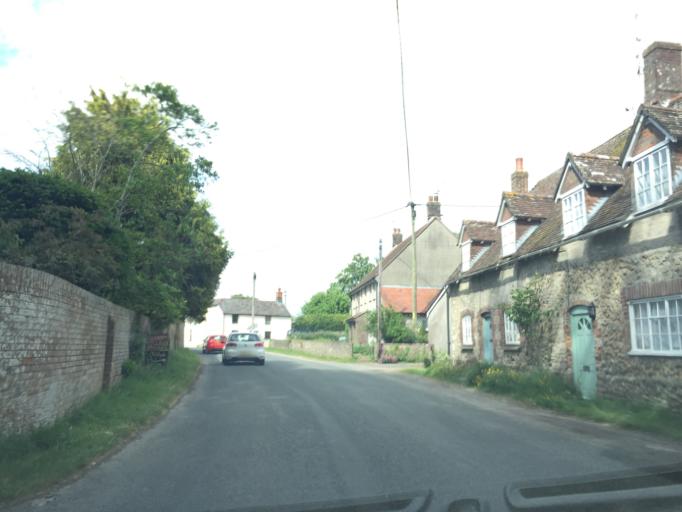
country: GB
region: England
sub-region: Dorset
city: Bovington Camp
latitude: 50.6605
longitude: -2.2748
